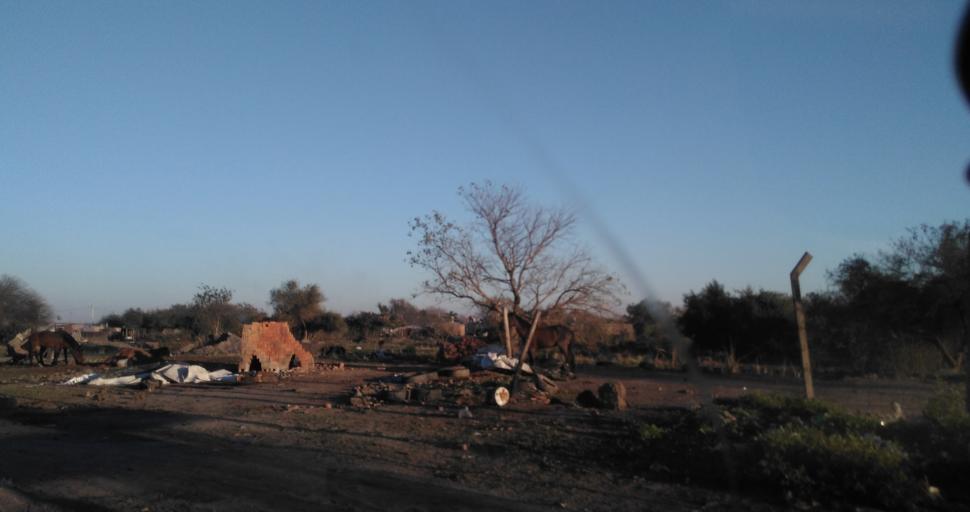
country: AR
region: Chaco
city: Fontana
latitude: -27.4333
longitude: -59.0310
